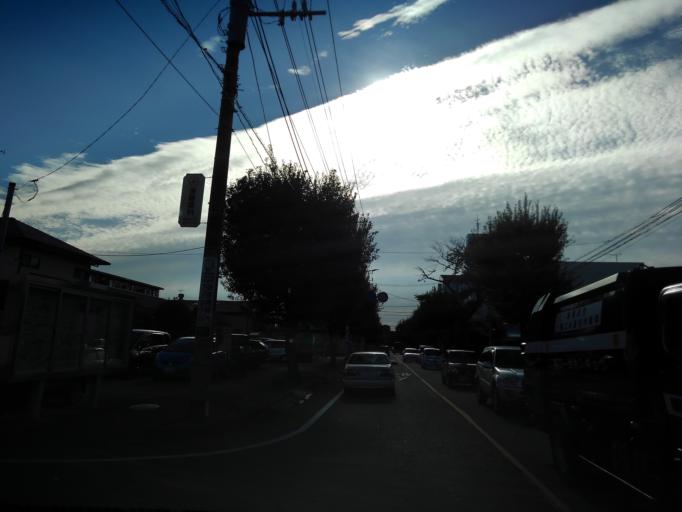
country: JP
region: Tokyo
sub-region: Machida-shi
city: Machida
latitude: 35.5725
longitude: 139.3996
